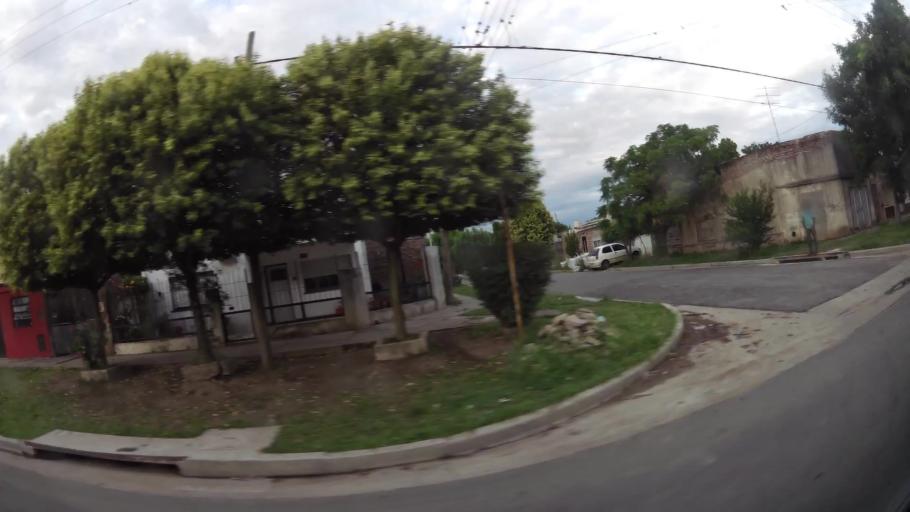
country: AR
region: Buenos Aires
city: San Nicolas de los Arroyos
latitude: -33.3247
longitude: -60.2391
